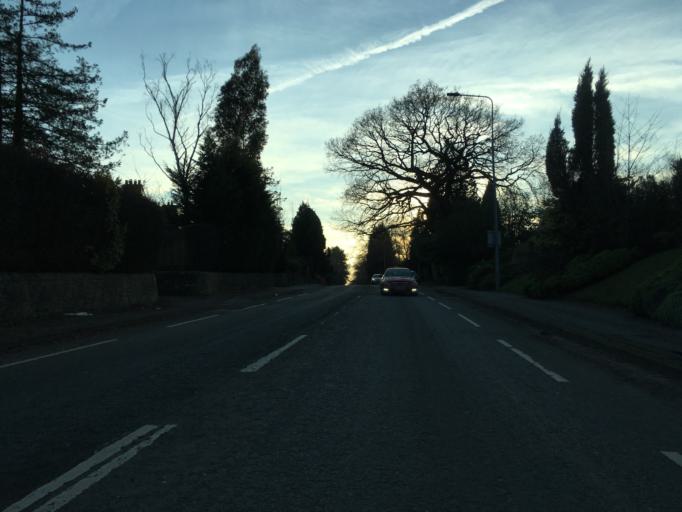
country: GB
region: England
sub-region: Cheshire East
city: Wilmslow
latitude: 53.3420
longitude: -2.2204
